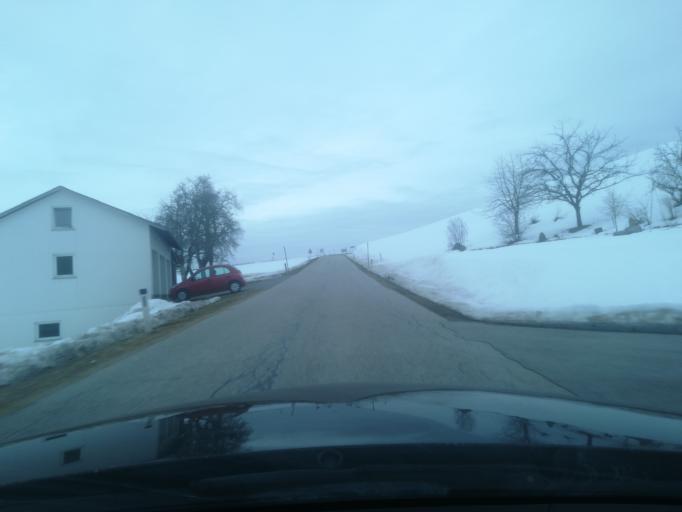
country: AT
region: Upper Austria
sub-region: Politischer Bezirk Perg
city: Perg
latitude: 48.3715
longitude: 14.6356
